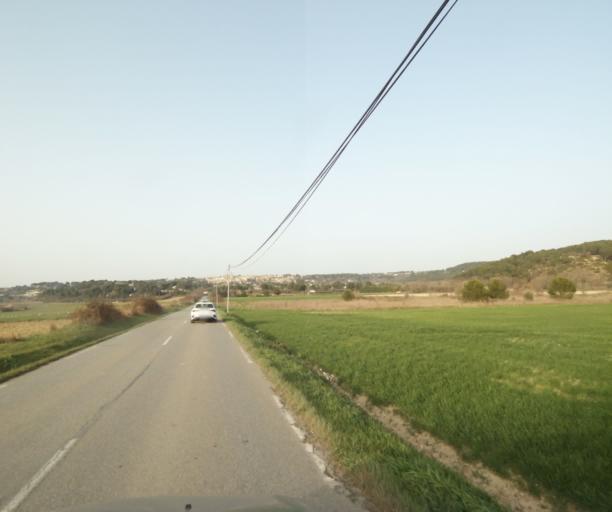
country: FR
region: Provence-Alpes-Cote d'Azur
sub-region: Departement des Bouches-du-Rhone
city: Eguilles
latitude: 43.5539
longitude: 5.3501
